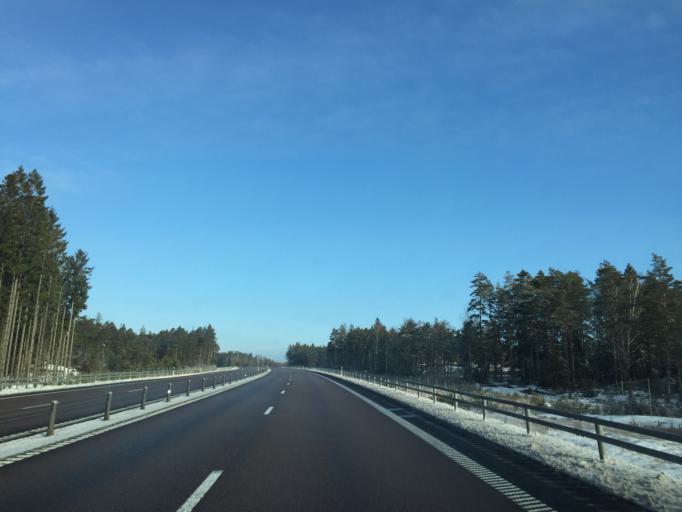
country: SE
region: Vaestra Goetaland
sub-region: Tanums Kommun
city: Tanumshede
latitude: 58.7852
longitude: 11.2776
